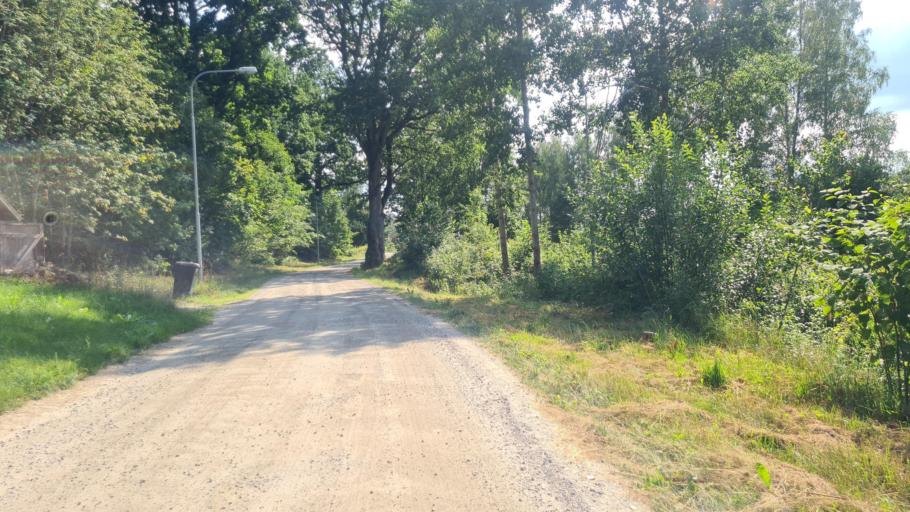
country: SE
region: Kronoberg
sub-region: Ljungby Kommun
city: Ljungby
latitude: 56.7389
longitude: 13.8745
